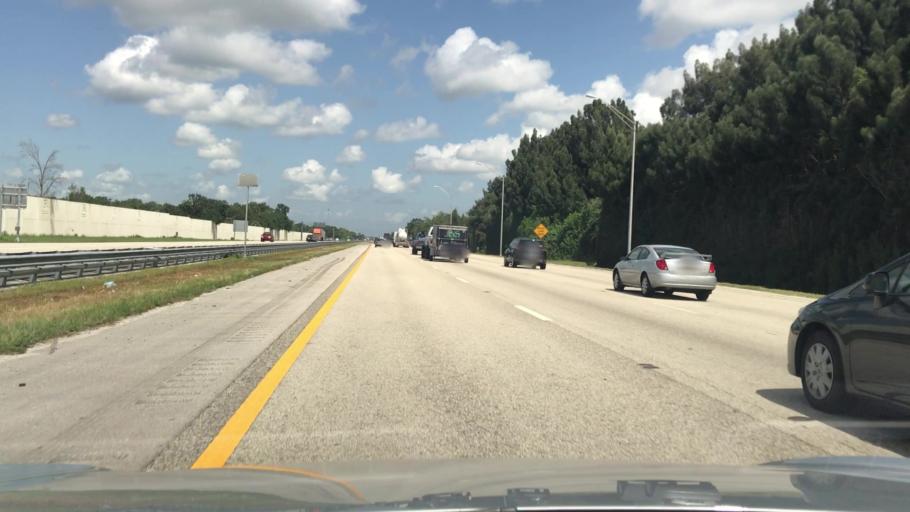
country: US
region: Florida
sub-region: Brevard County
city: Palm Bay
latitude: 28.0051
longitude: -80.6425
